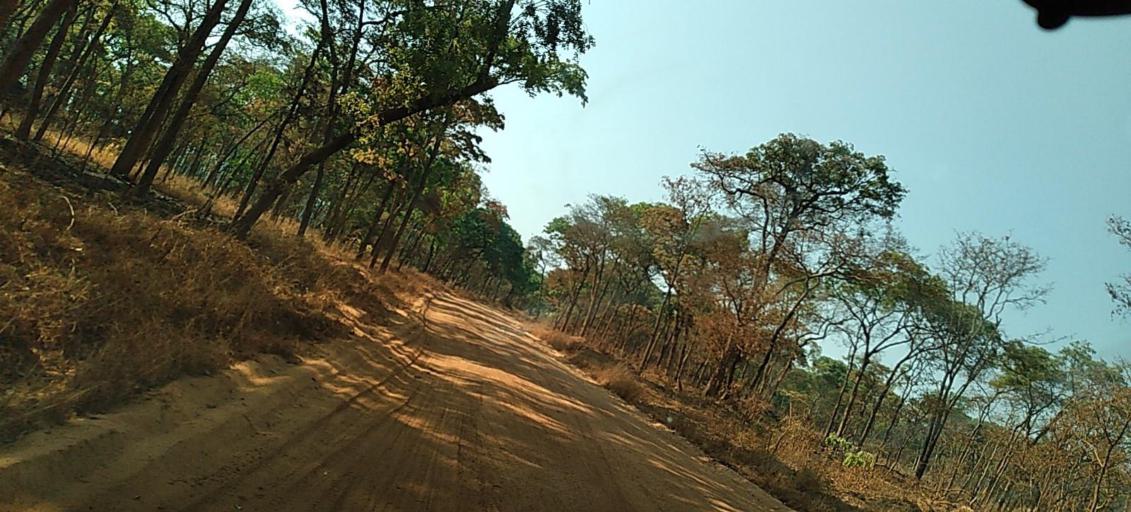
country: ZM
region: North-Western
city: Kasempa
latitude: -13.6662
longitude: 26.0125
